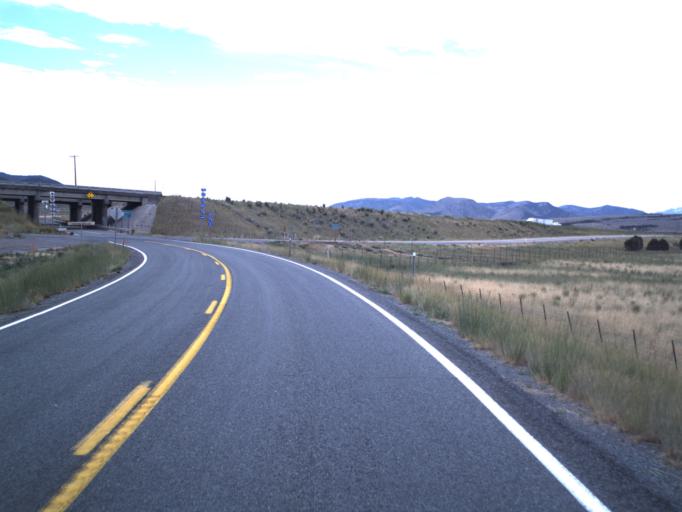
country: US
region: Utah
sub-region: Beaver County
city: Beaver
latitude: 38.5885
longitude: -112.5845
